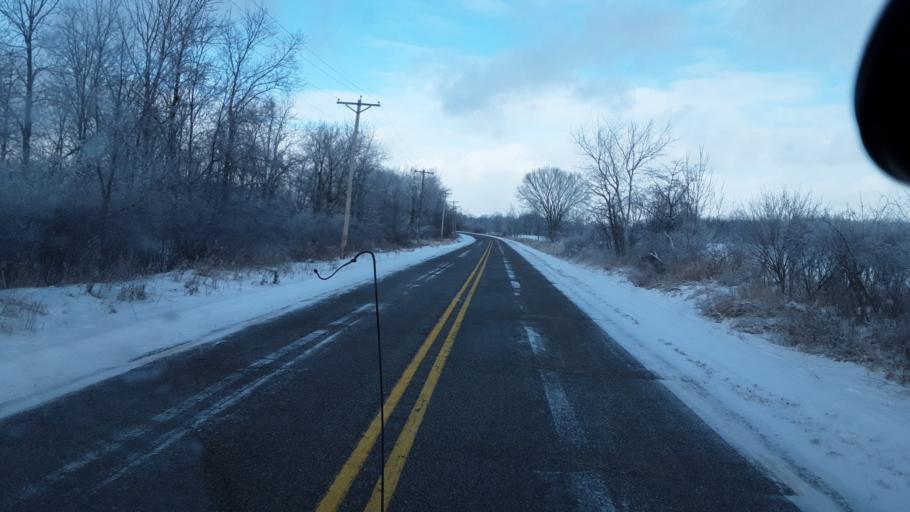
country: US
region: Michigan
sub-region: Eaton County
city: Eaton Rapids
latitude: 42.4881
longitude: -84.6212
